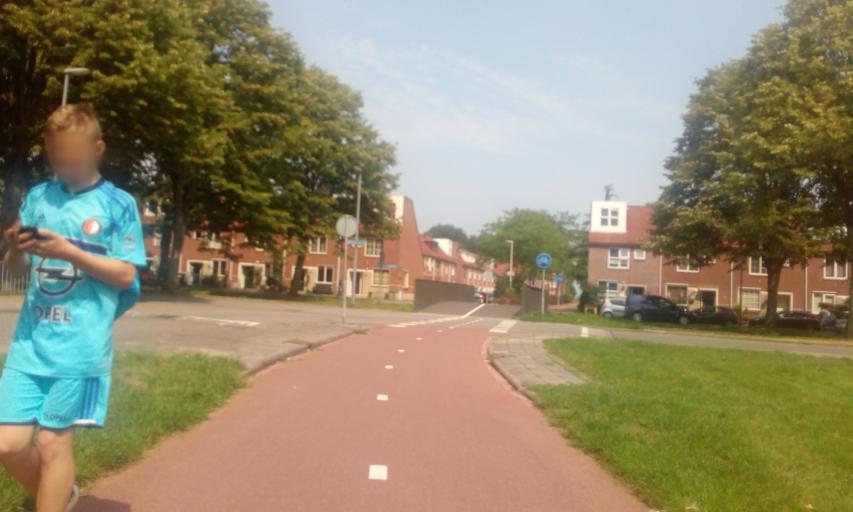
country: NL
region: South Holland
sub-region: Gemeente Capelle aan den IJssel
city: Capelle aan den IJssel
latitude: 51.9692
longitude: 4.5728
